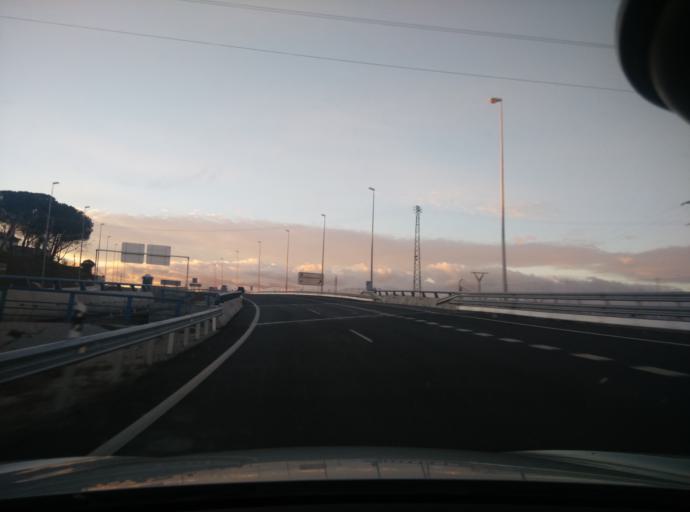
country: ES
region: Madrid
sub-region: Provincia de Madrid
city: Tres Cantos
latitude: 40.6141
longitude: -3.7251
